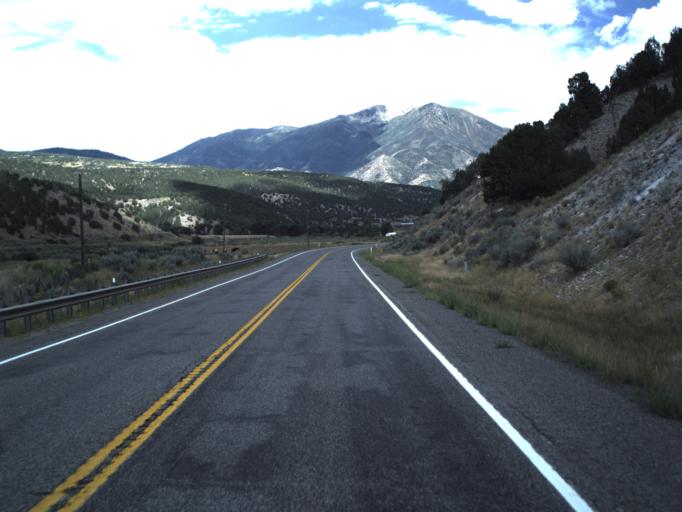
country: US
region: Utah
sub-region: Utah County
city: Woodland Hills
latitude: 39.8791
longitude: -111.5425
